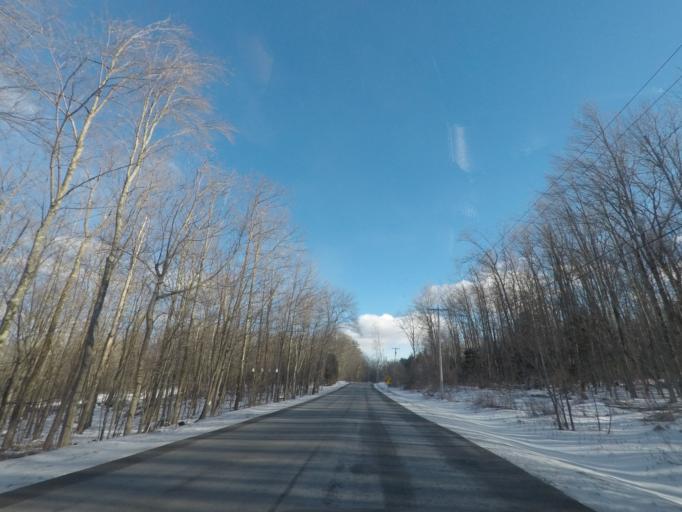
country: US
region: New York
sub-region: Rensselaer County
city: Hoosick Falls
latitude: 42.7894
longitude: -73.3995
